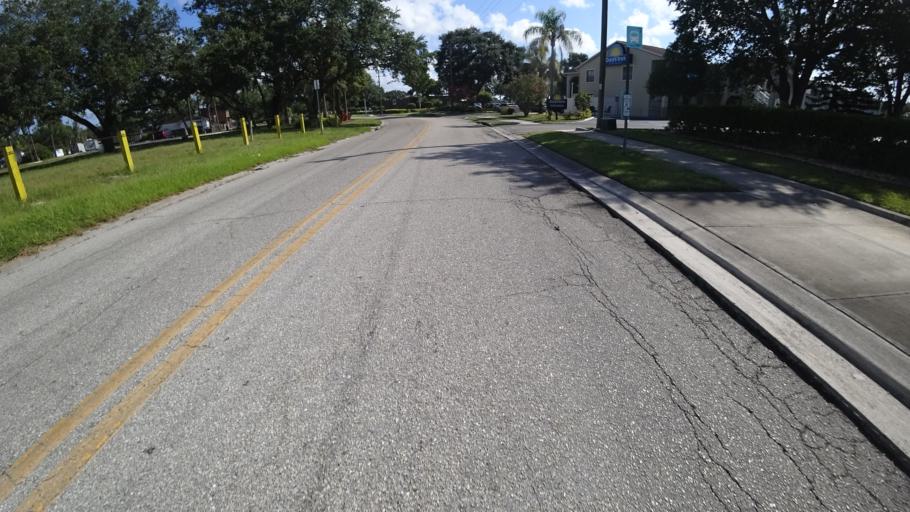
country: US
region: Florida
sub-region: Manatee County
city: Ellenton
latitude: 27.4930
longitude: -82.4756
